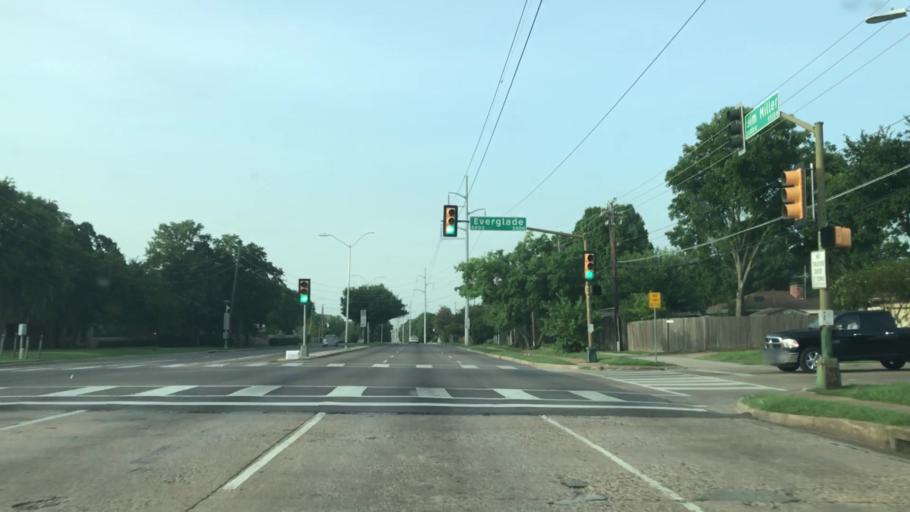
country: US
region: Texas
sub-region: Dallas County
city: Balch Springs
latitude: 32.7856
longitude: -96.7002
